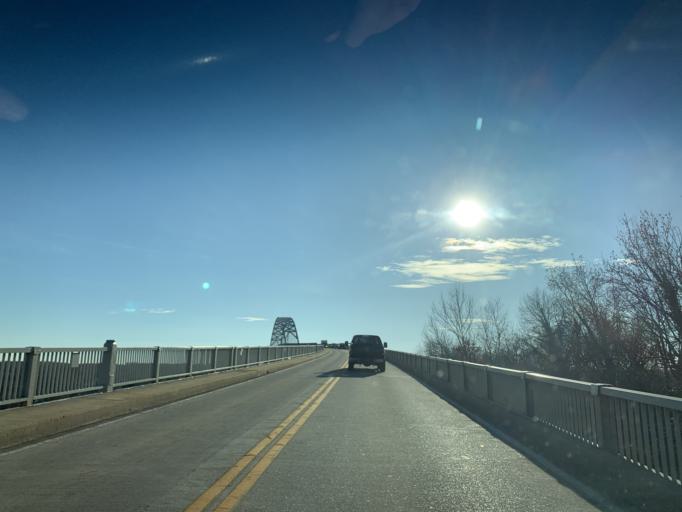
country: US
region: Maryland
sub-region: Cecil County
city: Elkton
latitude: 39.5334
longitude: -75.8118
